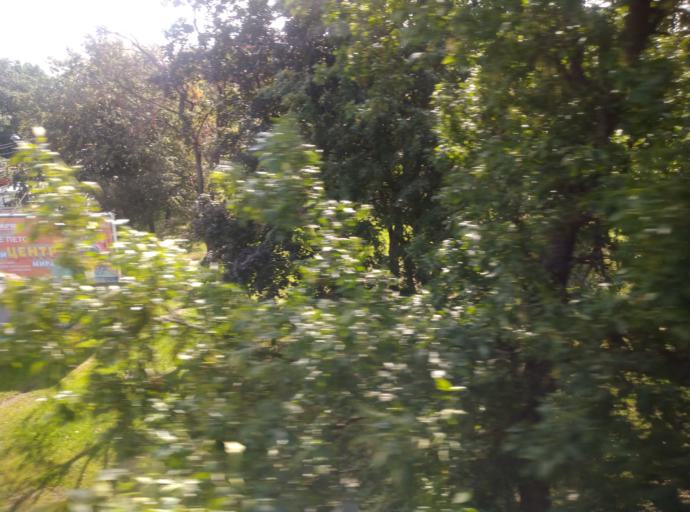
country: RU
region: St.-Petersburg
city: Centralniy
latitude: 59.9138
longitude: 30.4043
